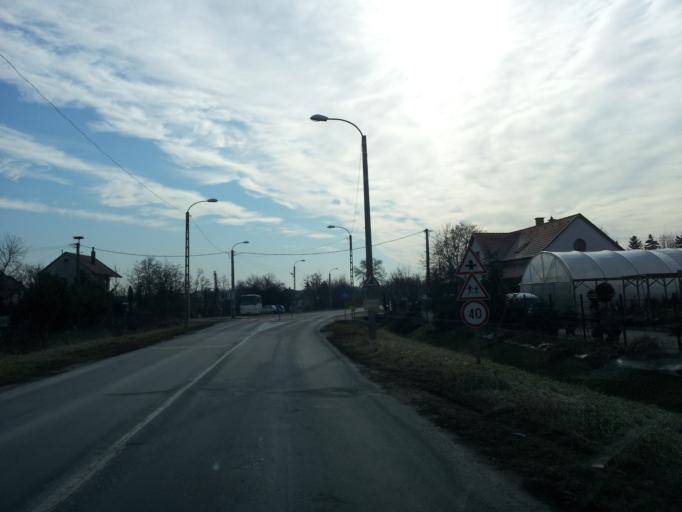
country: HU
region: Fejer
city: Kapolnasnyek
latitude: 47.2365
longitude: 18.6721
